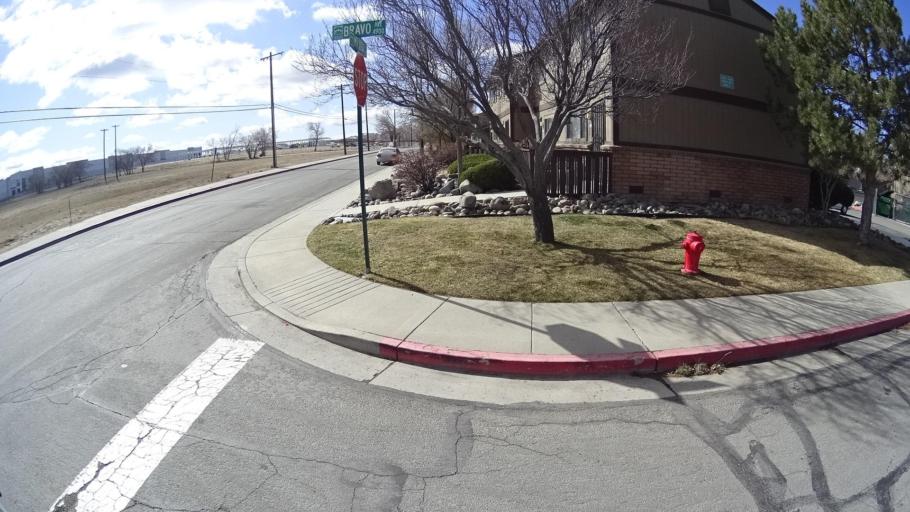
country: US
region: Nevada
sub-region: Washoe County
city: Lemmon Valley
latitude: 39.6574
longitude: -119.8741
